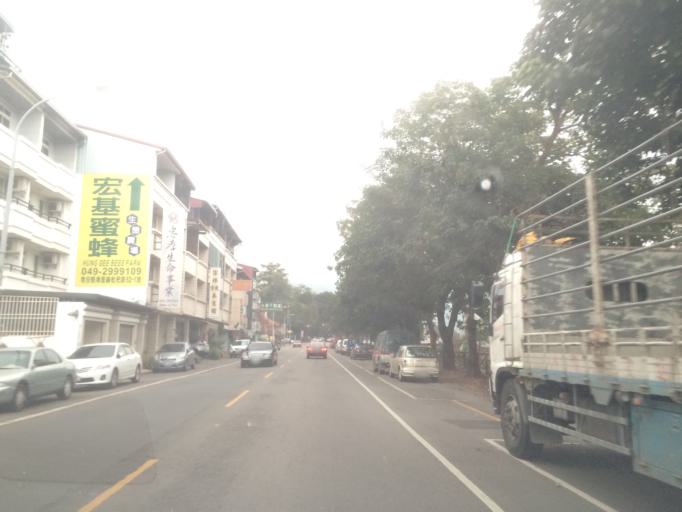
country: TW
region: Taiwan
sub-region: Nantou
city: Puli
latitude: 23.9589
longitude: 120.9655
